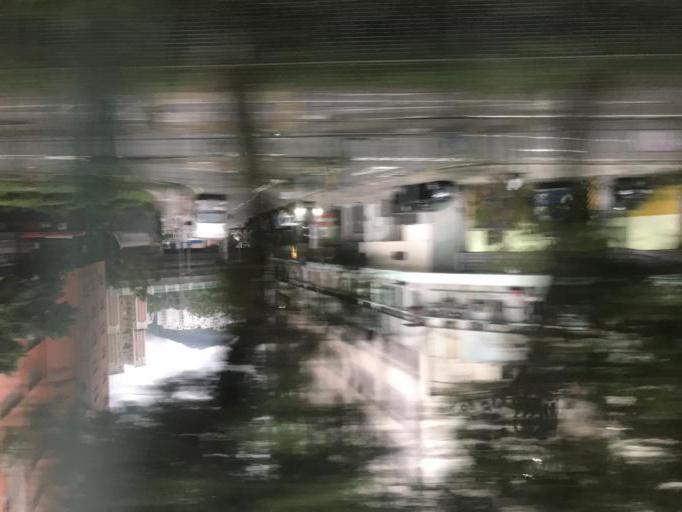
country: HK
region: Sha Tin
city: Sha Tin
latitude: 22.3761
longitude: 114.1822
